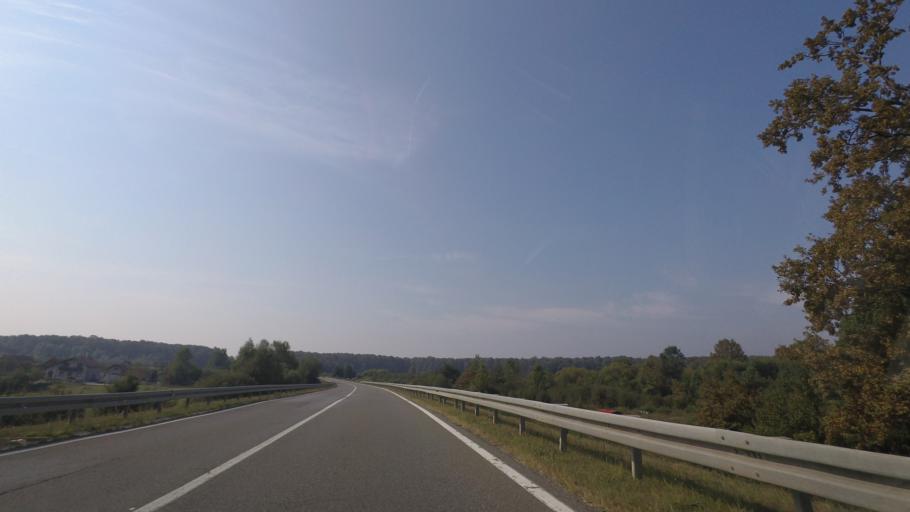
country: HR
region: Sisacko-Moslavacka
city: Novska
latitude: 45.3272
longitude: 16.9488
